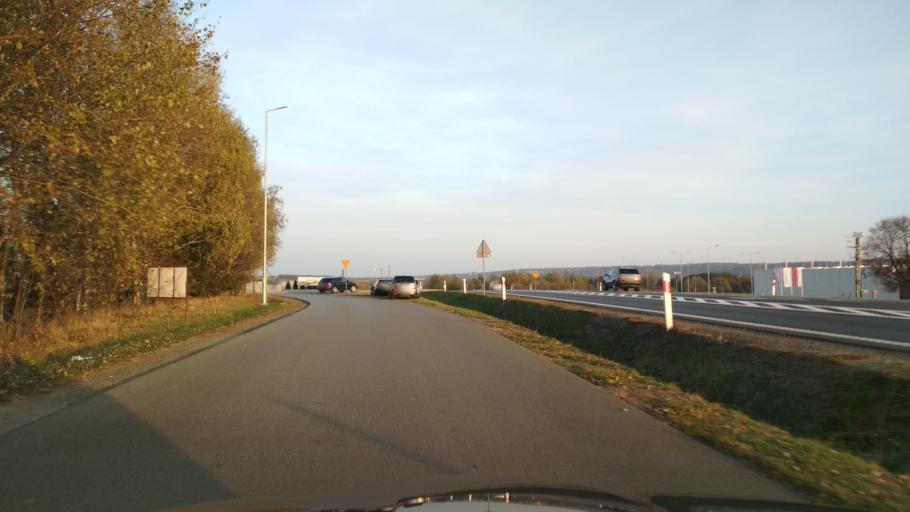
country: PL
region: Subcarpathian Voivodeship
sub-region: Powiat ropczycko-sedziszowski
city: Sedziszow Malopolski
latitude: 50.0625
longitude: 21.7129
